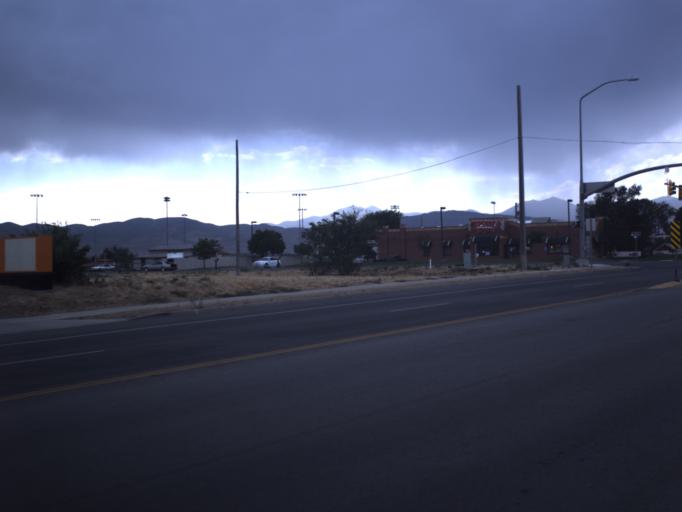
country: US
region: Utah
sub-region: Salt Lake County
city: Riverton
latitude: 40.5269
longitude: -111.9058
